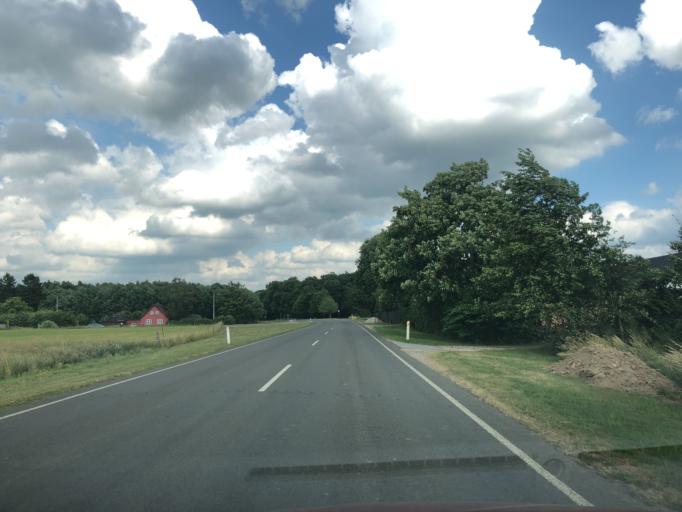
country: DK
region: Zealand
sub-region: Faxe Kommune
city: Fakse
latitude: 55.3143
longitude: 12.1374
